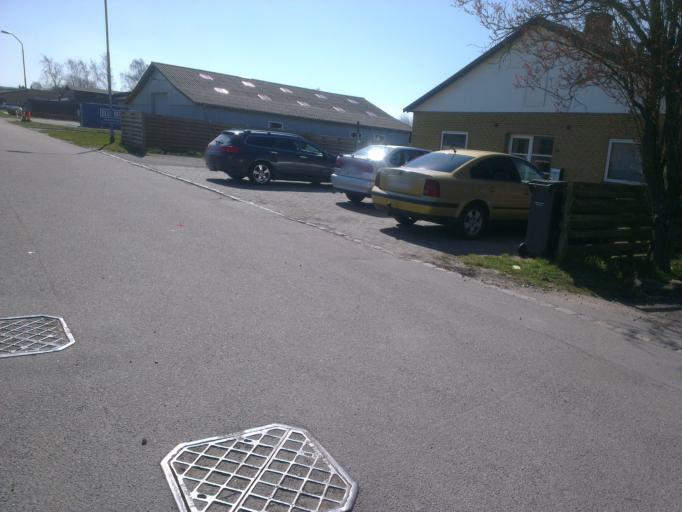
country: DK
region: Capital Region
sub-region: Frederikssund Kommune
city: Frederikssund
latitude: 55.8521
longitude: 12.0652
